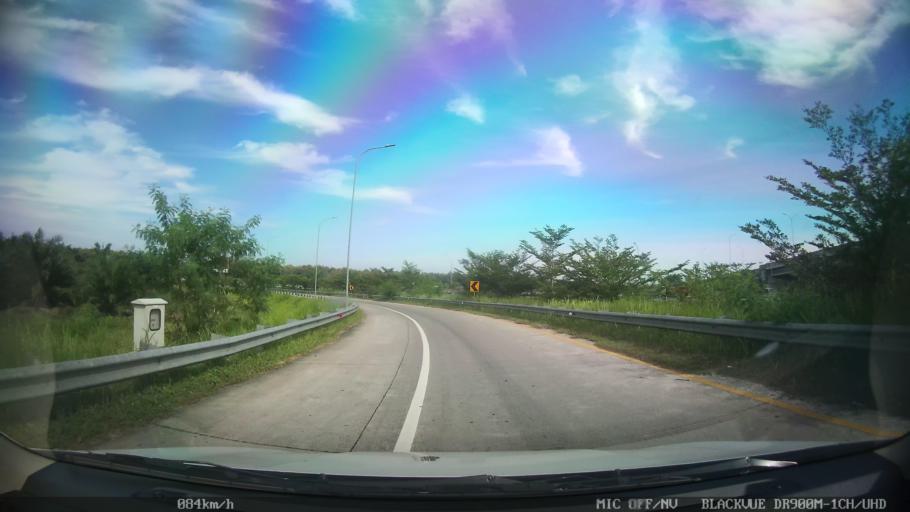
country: ID
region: North Sumatra
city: Medan
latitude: 3.6363
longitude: 98.6365
